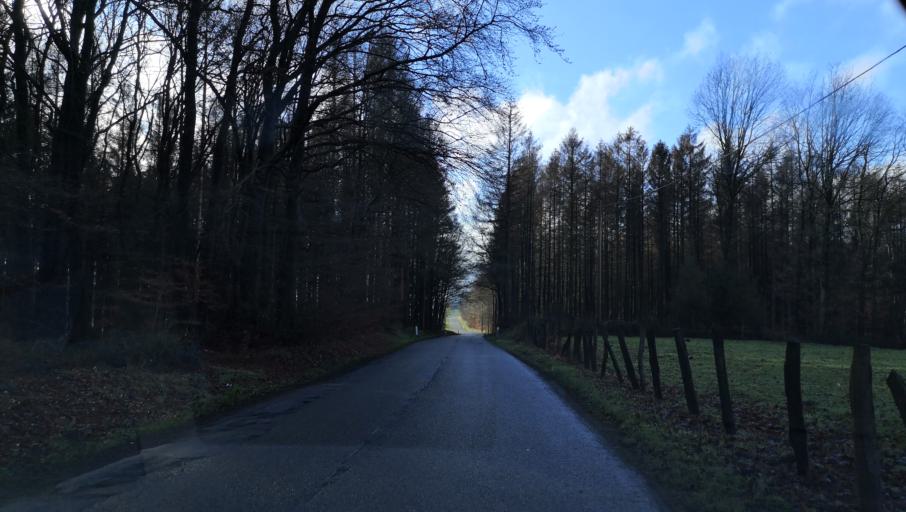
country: DE
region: North Rhine-Westphalia
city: Radevormwald
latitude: 51.2326
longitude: 7.3483
